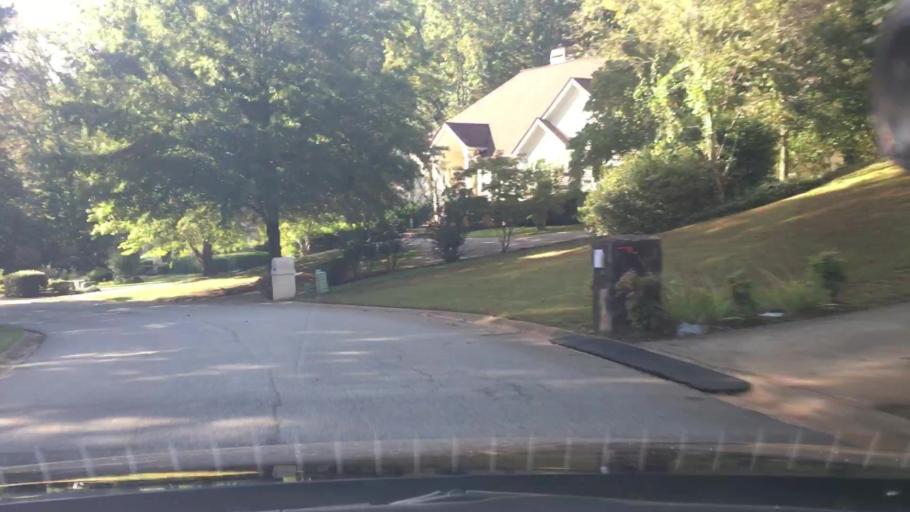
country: US
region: Georgia
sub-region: Coweta County
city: East Newnan
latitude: 33.3991
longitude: -84.7164
